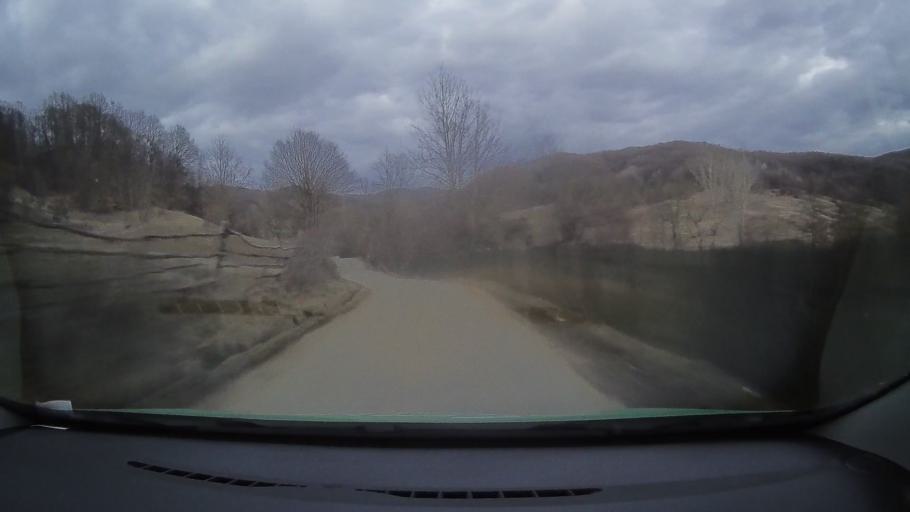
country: RO
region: Prahova
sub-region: Comuna Adunati
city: Adunati
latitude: 45.1186
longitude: 25.5948
